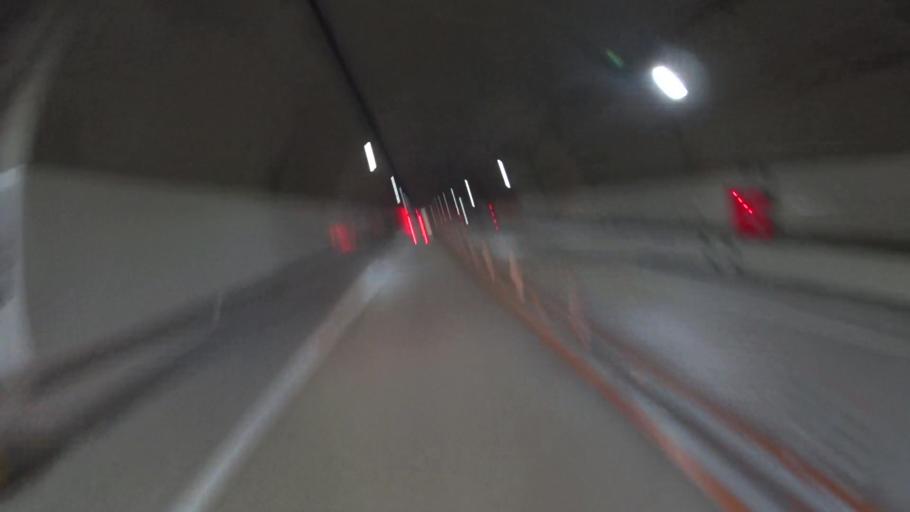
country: JP
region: Kyoto
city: Ayabe
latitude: 35.2459
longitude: 135.3433
